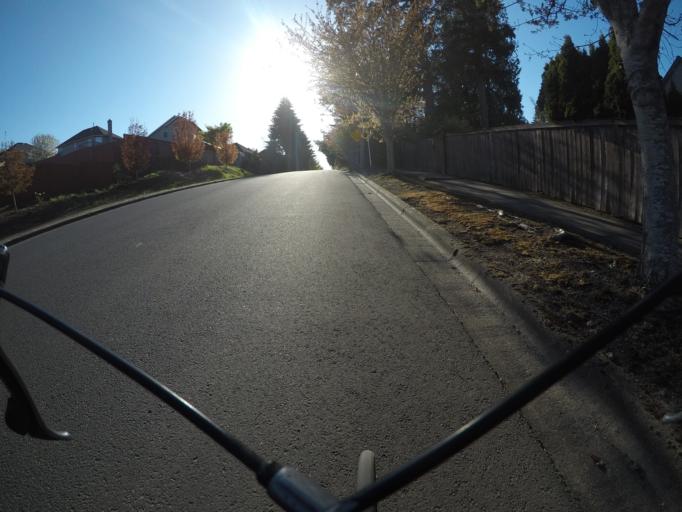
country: US
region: Oregon
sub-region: Washington County
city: Aloha
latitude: 45.4621
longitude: -122.8637
